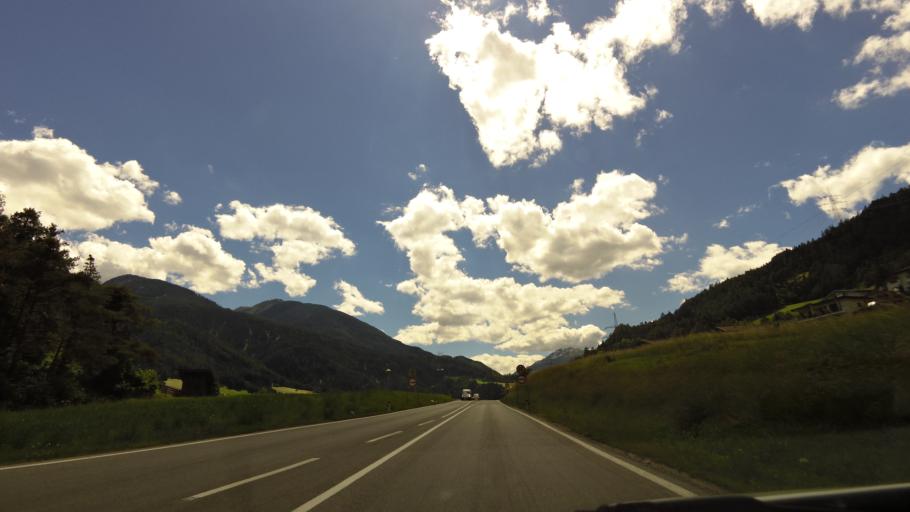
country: AT
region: Tyrol
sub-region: Politischer Bezirk Imst
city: Roppen
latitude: 47.2222
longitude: 10.8161
